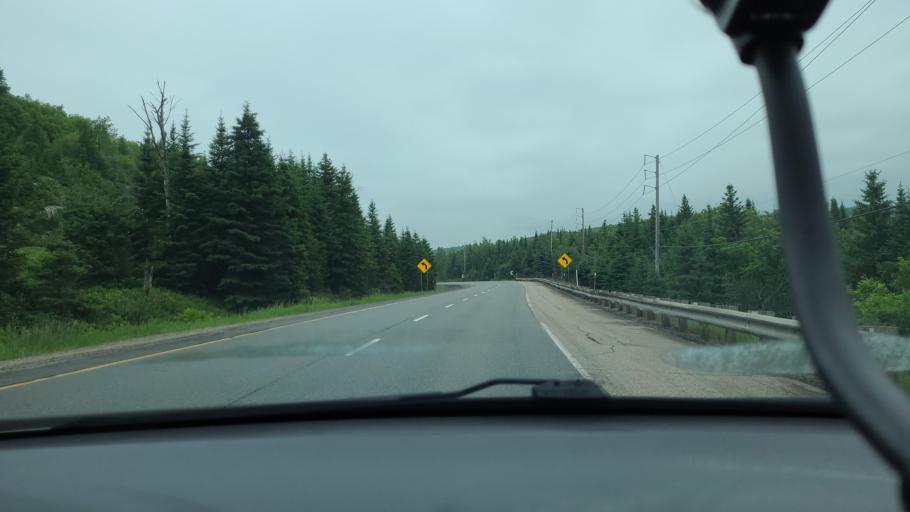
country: CA
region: Quebec
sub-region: Laurentides
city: Sainte-Agathe-des-Monts
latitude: 46.1076
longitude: -74.4172
